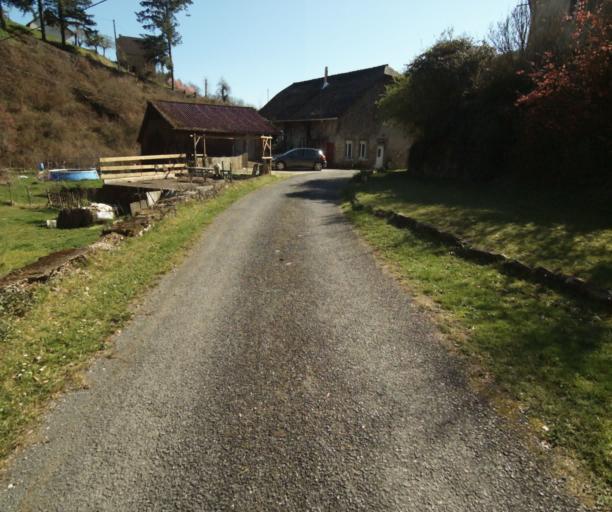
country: FR
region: Limousin
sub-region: Departement de la Correze
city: Tulle
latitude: 45.2718
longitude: 1.7422
